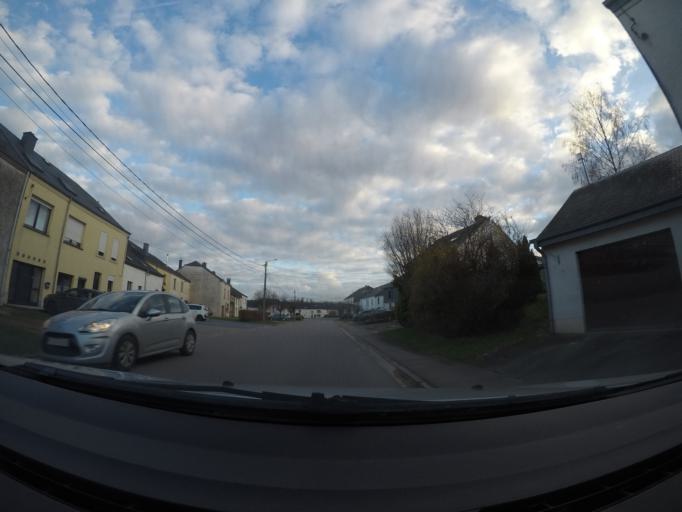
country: BE
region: Wallonia
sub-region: Province du Luxembourg
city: Etalle
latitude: 49.6707
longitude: 5.5637
